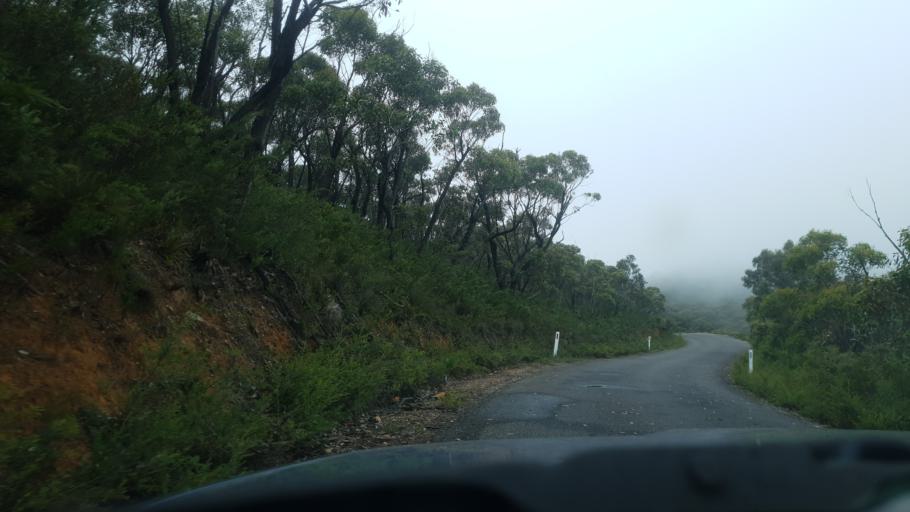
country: AU
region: Victoria
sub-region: Northern Grampians
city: Stawell
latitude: -37.2707
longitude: 142.5803
